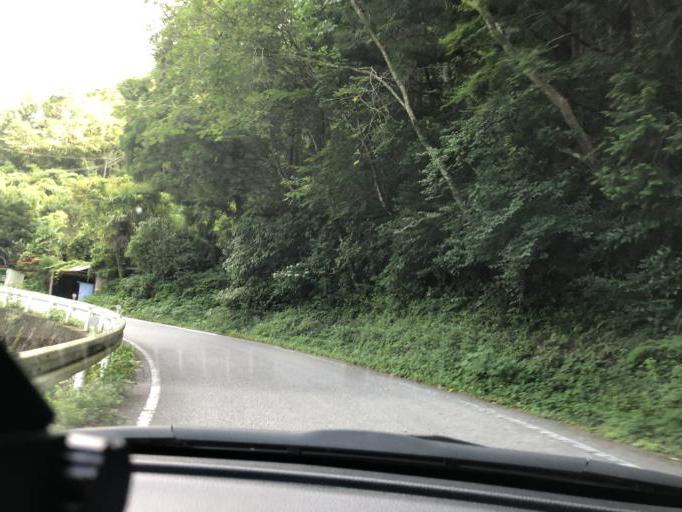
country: JP
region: Kochi
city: Kochi-shi
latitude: 33.6162
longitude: 133.4965
